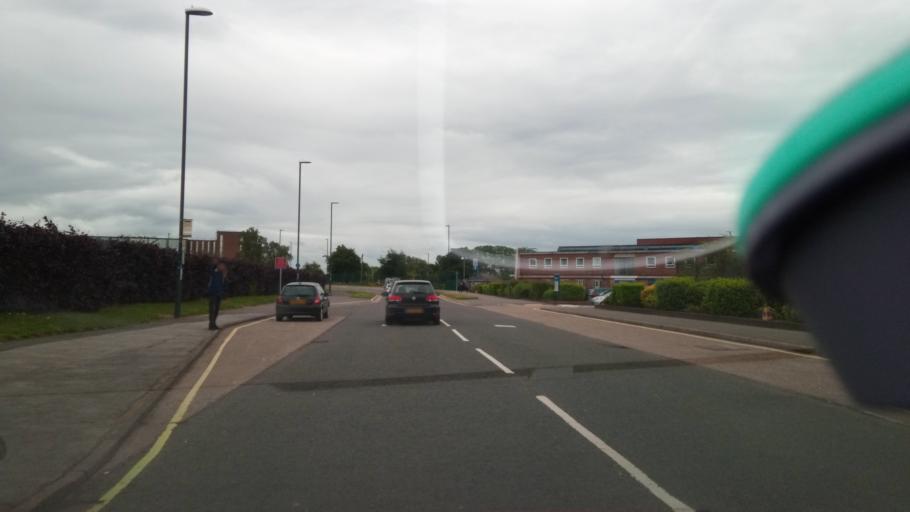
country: GB
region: England
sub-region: Derby
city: Derby
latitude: 52.8890
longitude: -1.4660
